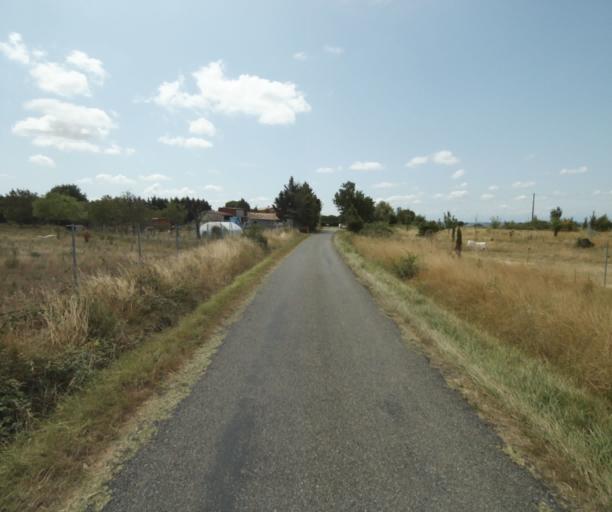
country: FR
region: Midi-Pyrenees
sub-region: Departement de la Haute-Garonne
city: Saint-Felix-Lauragais
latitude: 43.3982
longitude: 1.9089
